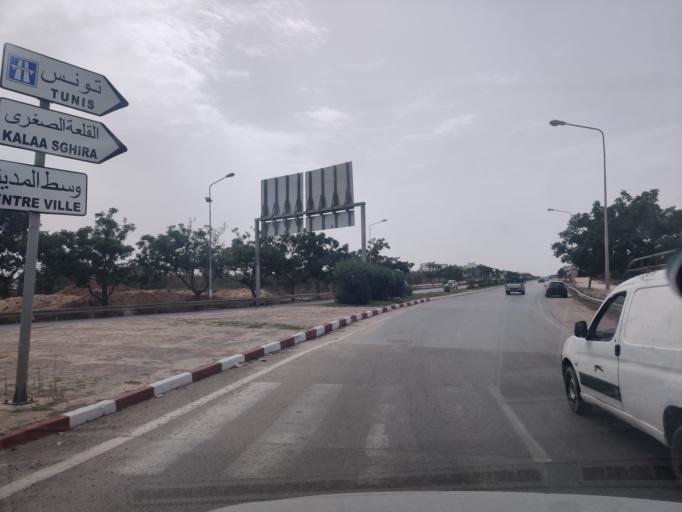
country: TN
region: Susah
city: Hammam Sousse
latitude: 35.8401
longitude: 10.5834
